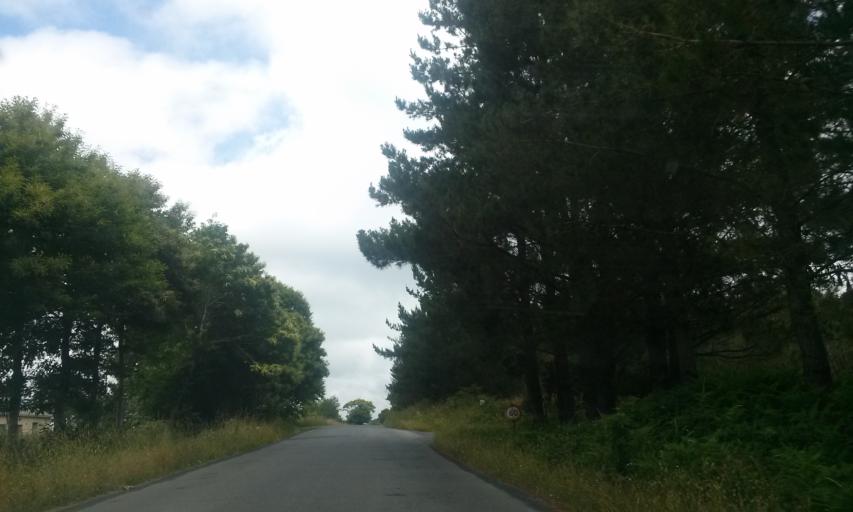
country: ES
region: Galicia
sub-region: Provincia de Lugo
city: Friol
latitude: 43.0813
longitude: -7.8157
